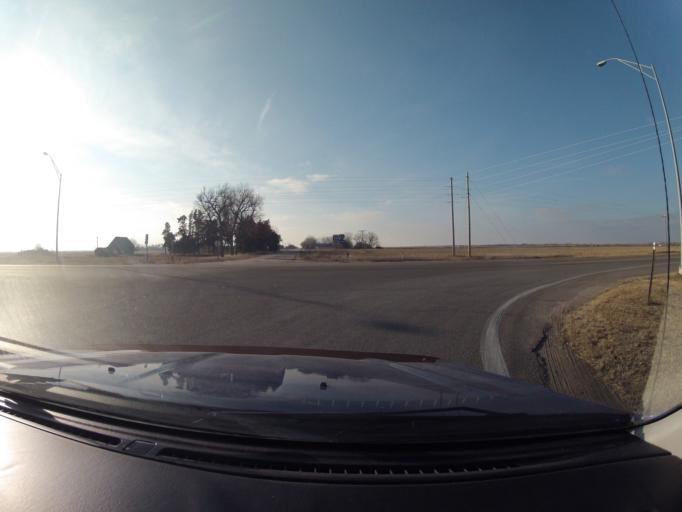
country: US
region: Nebraska
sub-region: Buffalo County
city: Kearney
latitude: 40.6410
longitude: -99.0846
